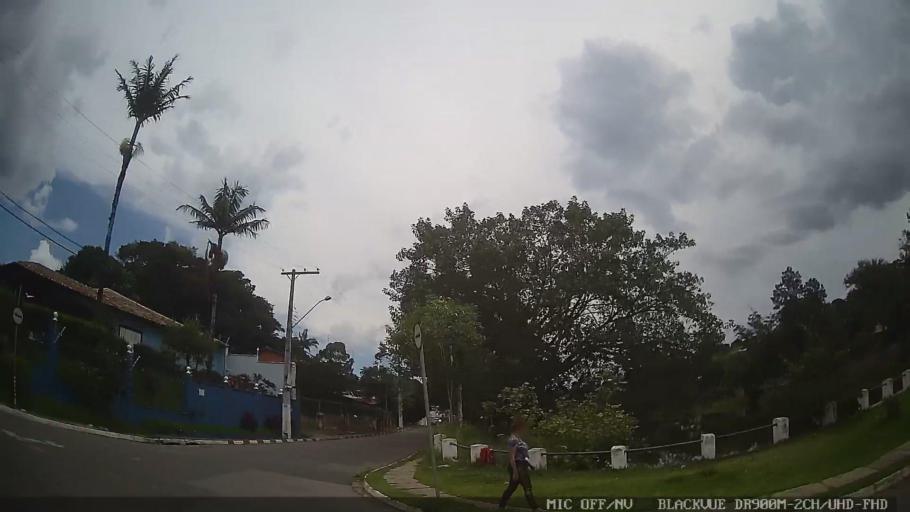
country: BR
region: Sao Paulo
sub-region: Atibaia
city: Atibaia
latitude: -23.1390
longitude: -46.5574
